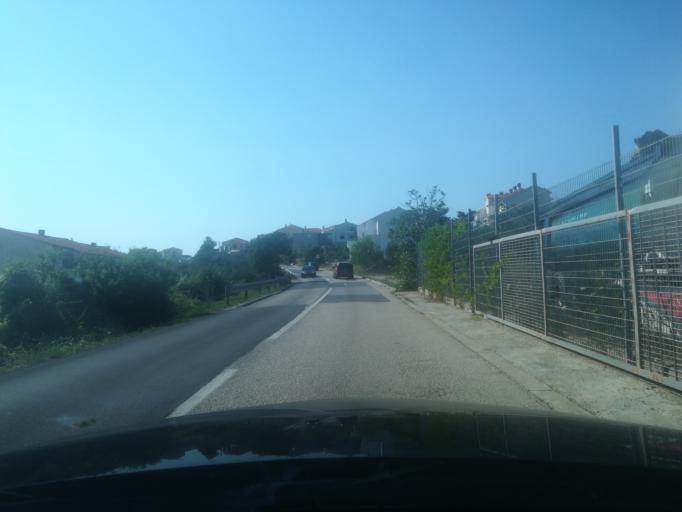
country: HR
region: Primorsko-Goranska
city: Banjol
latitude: 44.7340
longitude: 14.8087
